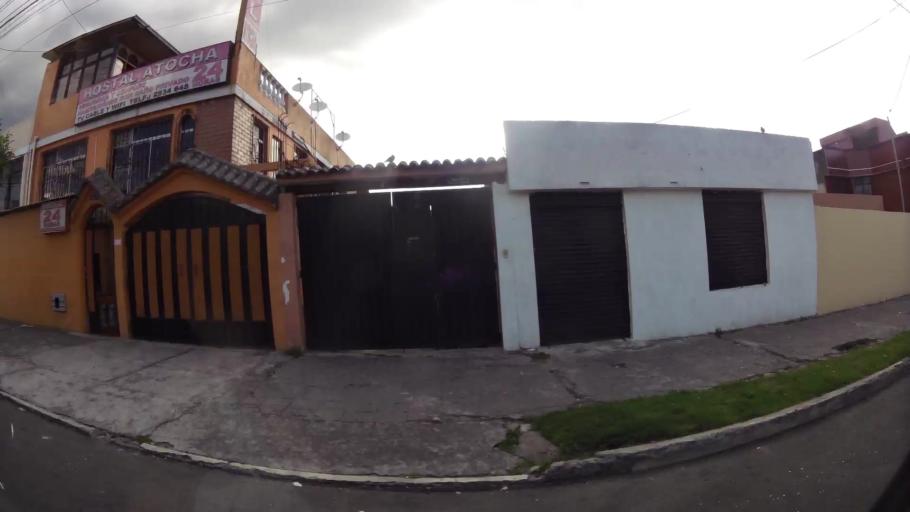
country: EC
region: Pichincha
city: Quito
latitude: -0.1195
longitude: -78.4890
